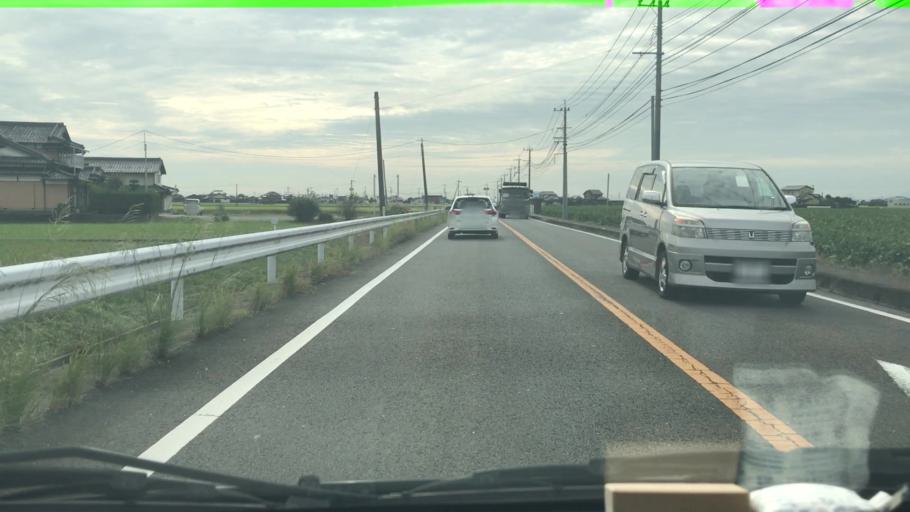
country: JP
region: Saga Prefecture
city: Takeocho-takeo
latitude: 33.2020
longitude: 130.0957
